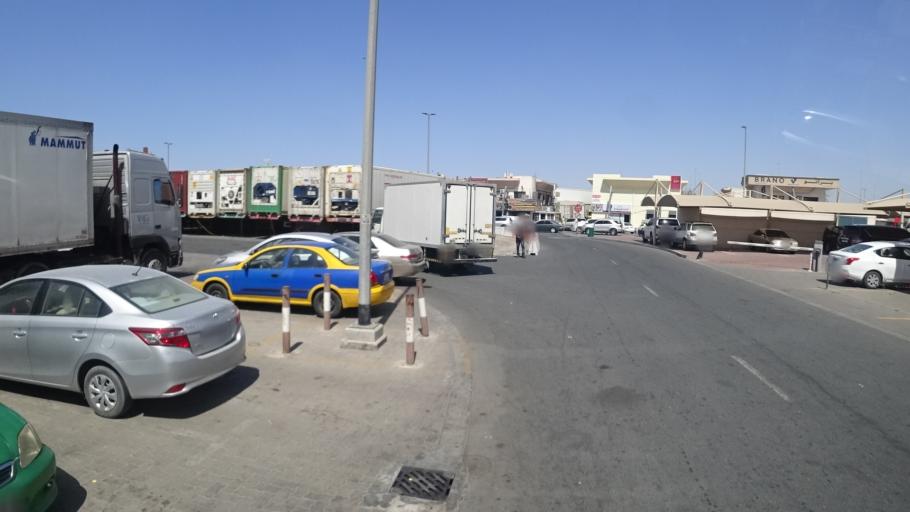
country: AE
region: Ash Shariqah
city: Sharjah
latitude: 25.1741
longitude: 55.3940
